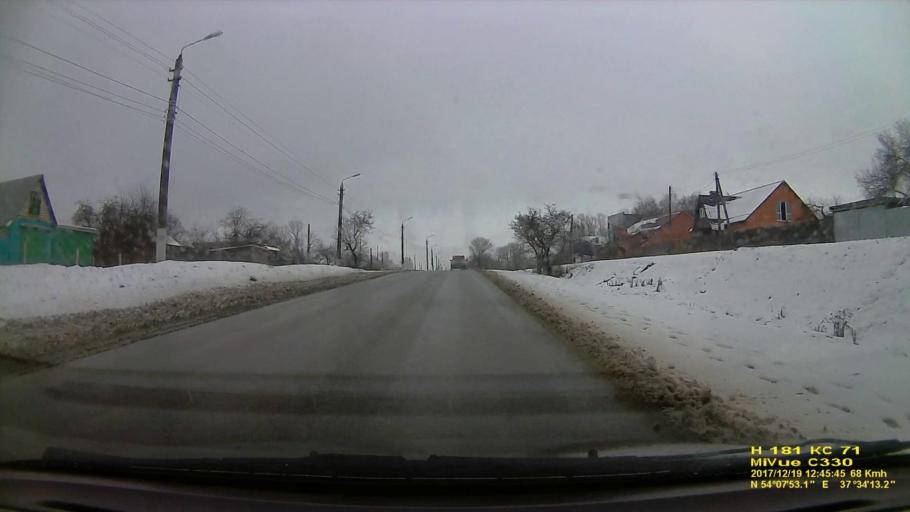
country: RU
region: Tula
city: Mendeleyevskiy
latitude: 54.1315
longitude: 37.5705
